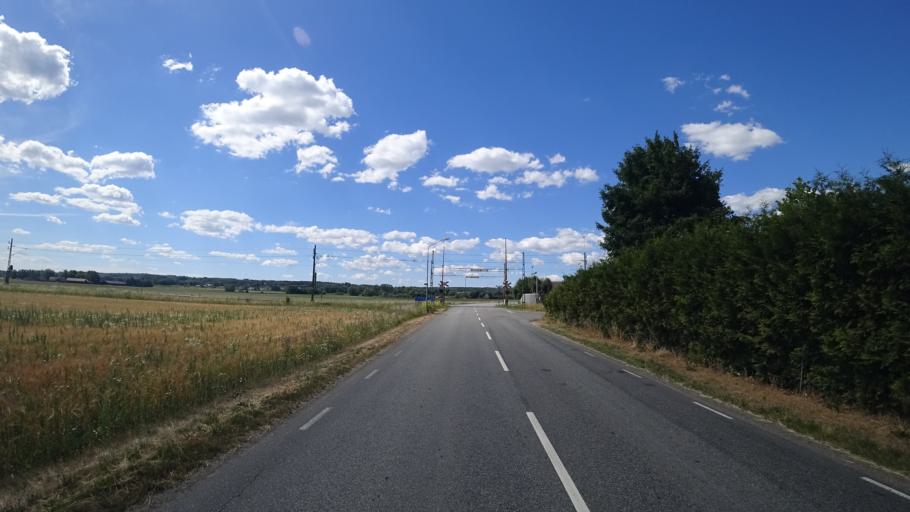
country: SE
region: Skane
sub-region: Kristianstads Kommun
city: Onnestad
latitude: 56.0585
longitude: 14.0345
